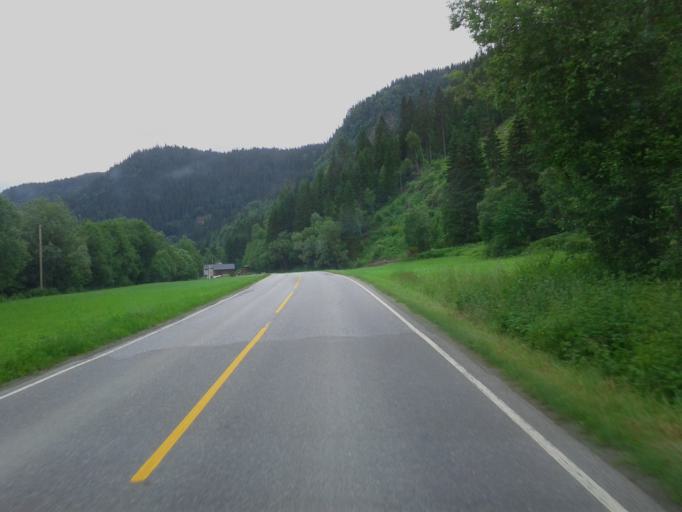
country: NO
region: Sor-Trondelag
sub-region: Midtre Gauldal
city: Storen
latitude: 63.0152
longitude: 10.3489
